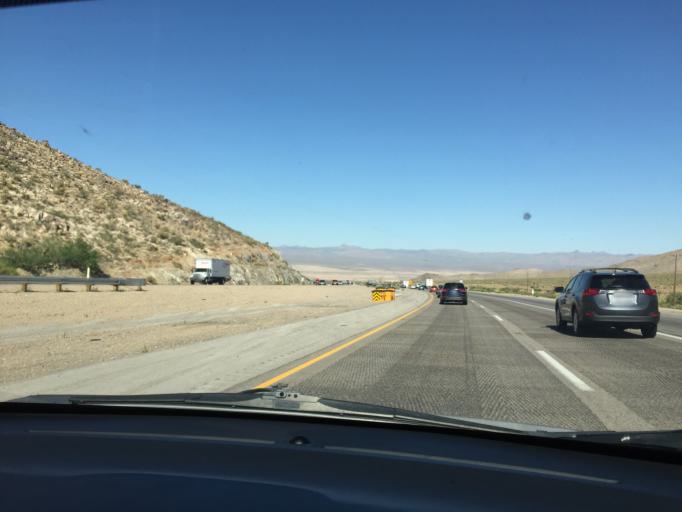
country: US
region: Nevada
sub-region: Clark County
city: Sandy Valley
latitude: 35.4611
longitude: -115.4736
